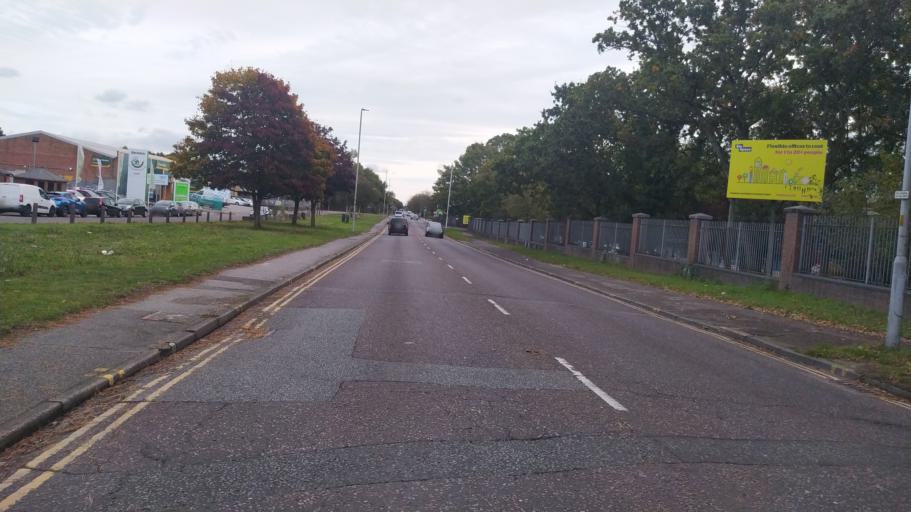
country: GB
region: England
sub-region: Dorset
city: Parkstone
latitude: 50.7522
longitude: -1.9285
